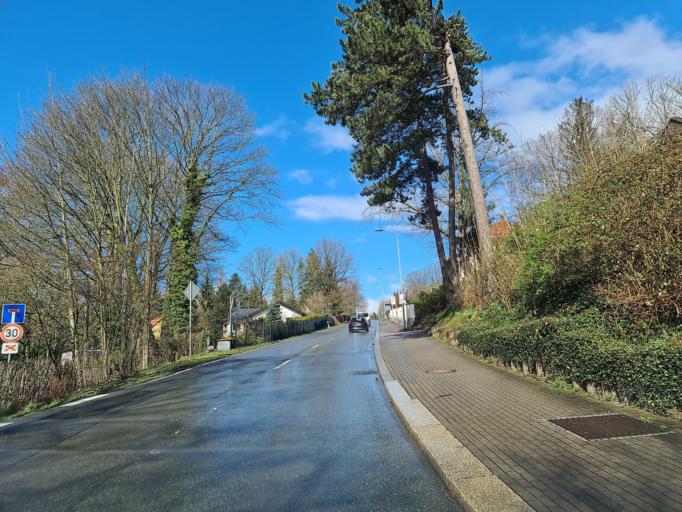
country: DE
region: Saxony
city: Hohenstein-Ernstthal
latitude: 50.8031
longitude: 12.6988
